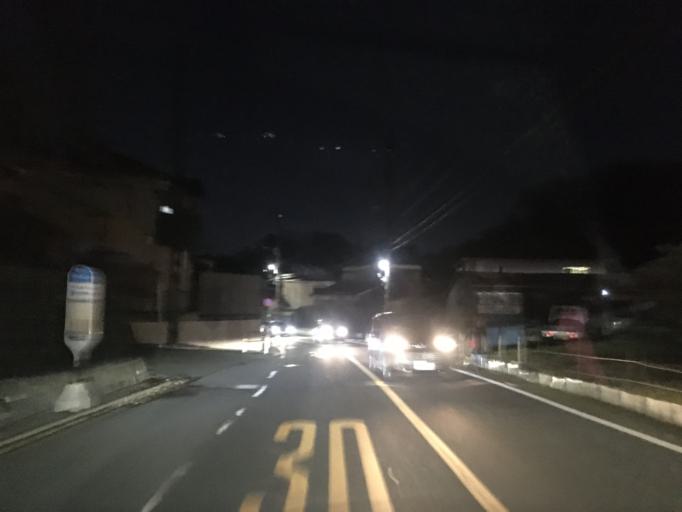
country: JP
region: Tokyo
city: Chofugaoka
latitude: 35.5868
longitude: 139.5219
